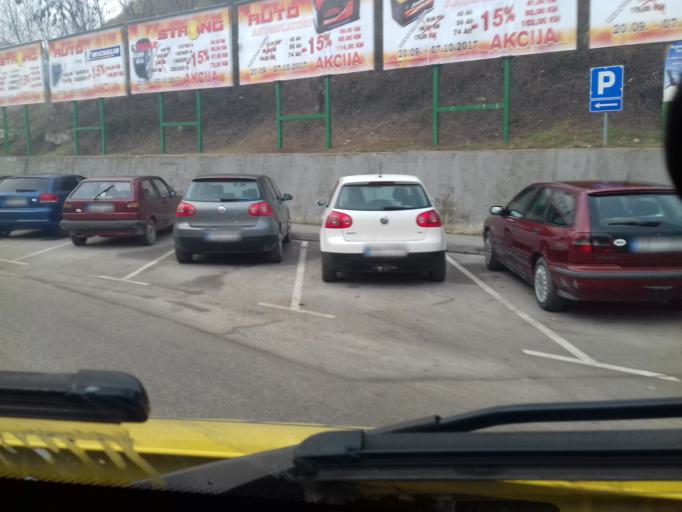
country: BA
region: Federation of Bosnia and Herzegovina
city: Kakanj
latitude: 44.1313
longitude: 18.1195
